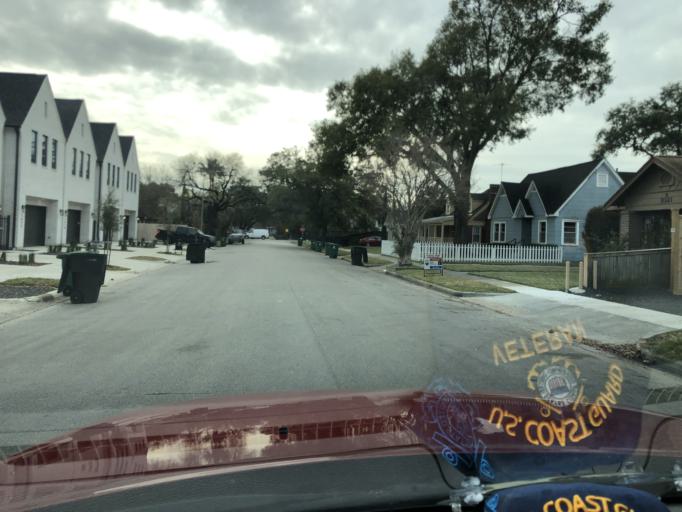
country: US
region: Texas
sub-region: Harris County
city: Houston
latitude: 29.7896
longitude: -95.4090
